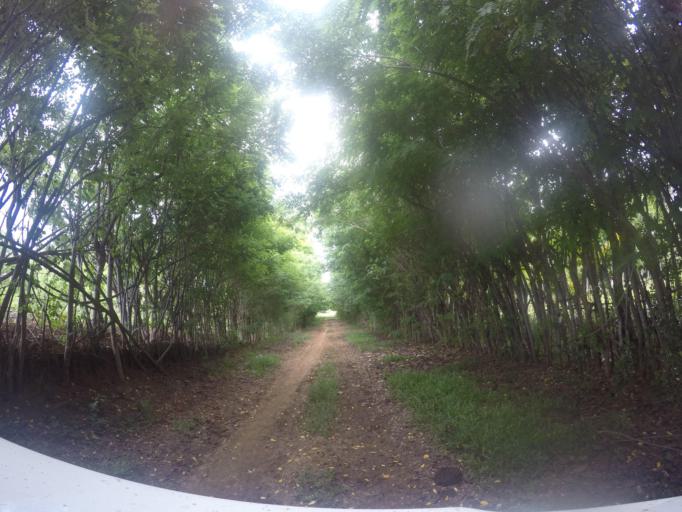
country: TL
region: Lautem
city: Lospalos
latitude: -8.5067
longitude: 127.0151
